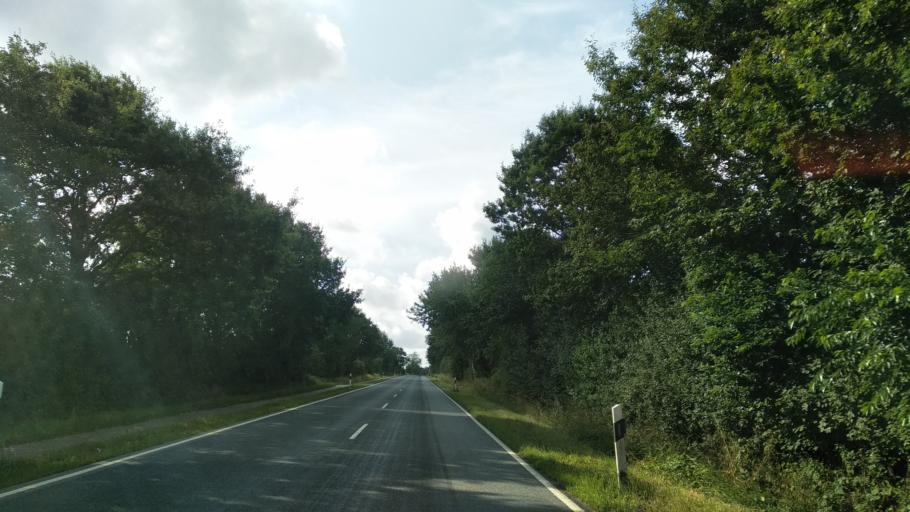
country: DE
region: Schleswig-Holstein
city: Selk
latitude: 54.4816
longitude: 9.5653
